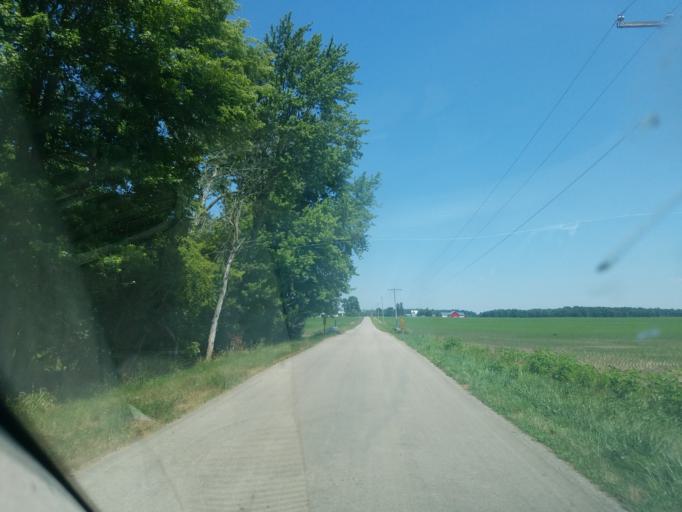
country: US
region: Ohio
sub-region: Mercer County
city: Rockford
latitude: 40.7361
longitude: -84.7370
